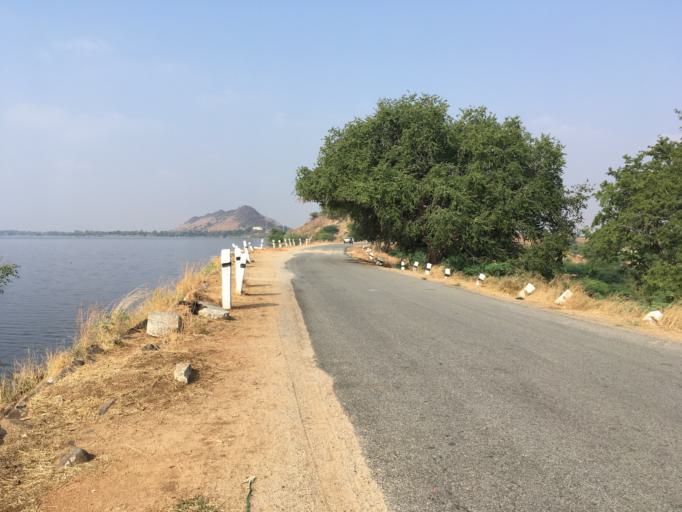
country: IN
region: Andhra Pradesh
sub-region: Anantapur
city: Puttaparthi
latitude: 14.1859
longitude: 77.7828
